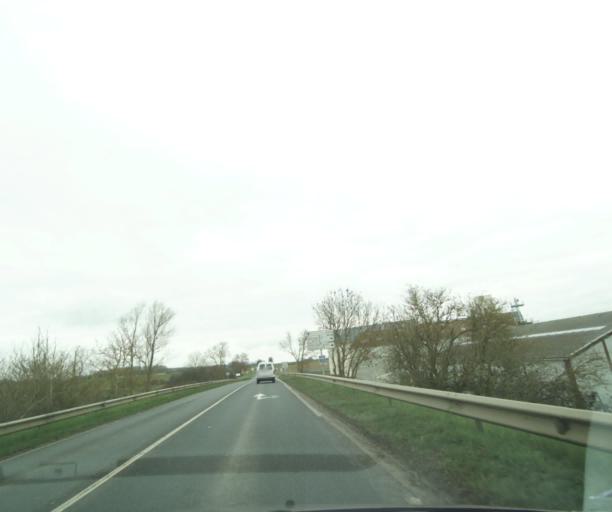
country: FR
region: Picardie
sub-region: Departement de l'Oise
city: Noyon
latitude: 49.5945
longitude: 2.9786
